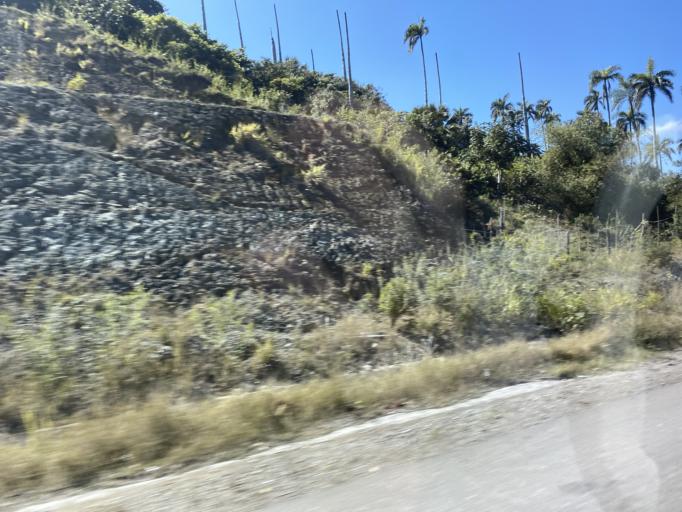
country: DO
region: Puerto Plata
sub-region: Puerto Plata
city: Puerto Plata
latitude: 19.8279
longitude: -70.7603
